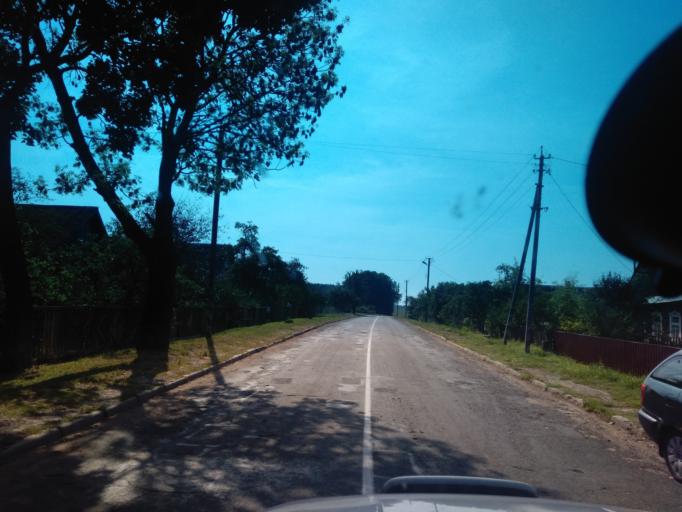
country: BY
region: Minsk
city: Uzda
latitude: 53.3891
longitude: 27.2428
